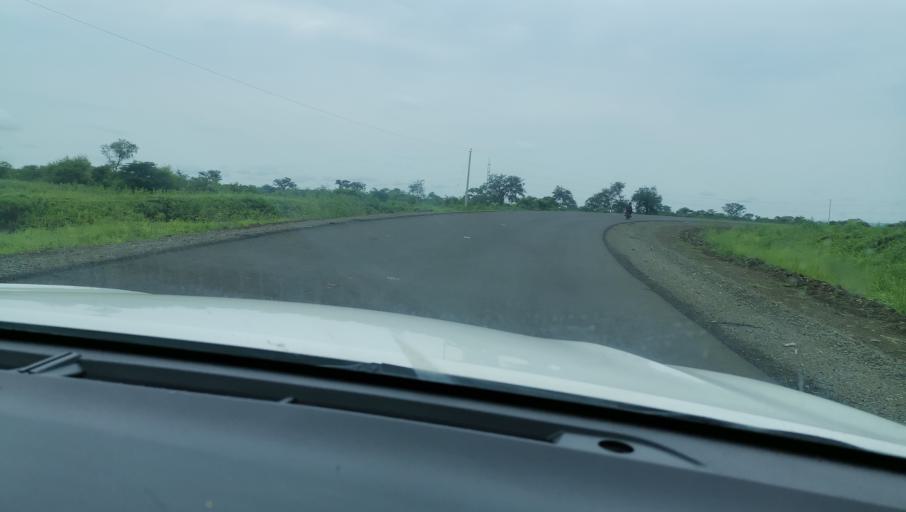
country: SD
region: Al Qadarif
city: Doka
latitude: 12.8998
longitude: 36.2199
